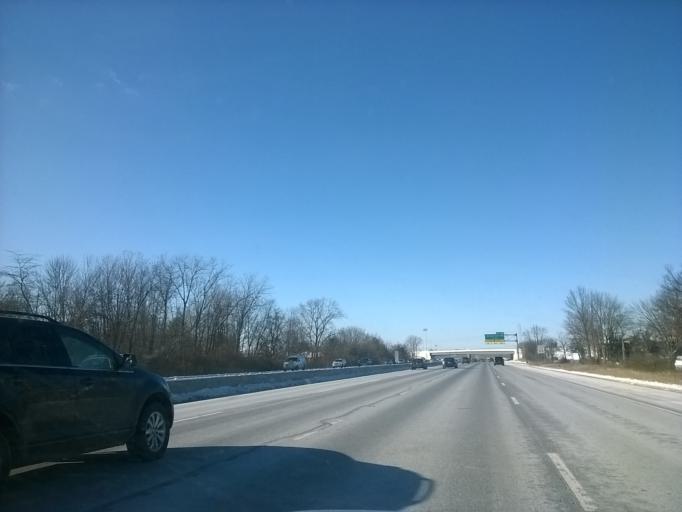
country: US
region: Indiana
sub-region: Hamilton County
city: Fishers
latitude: 39.9024
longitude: -86.0656
